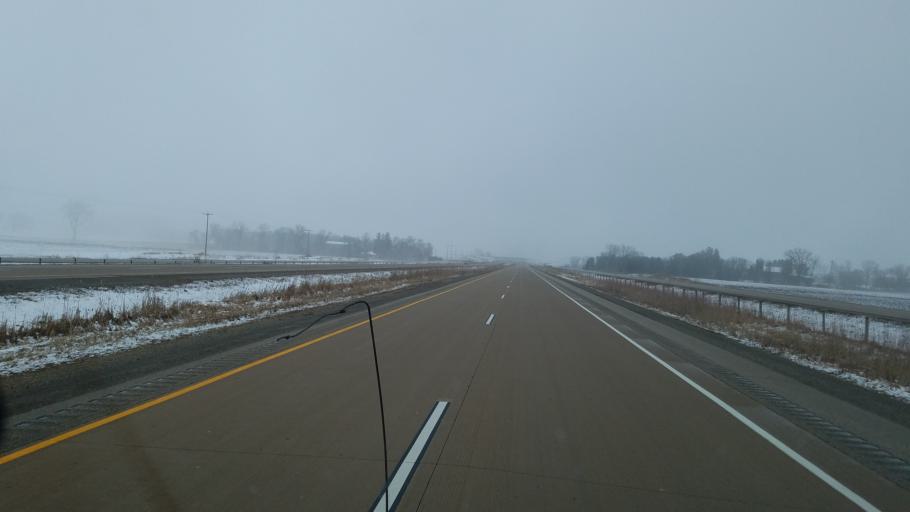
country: US
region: Wisconsin
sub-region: Winnebago County
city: Winneconne
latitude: 44.1582
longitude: -88.6641
